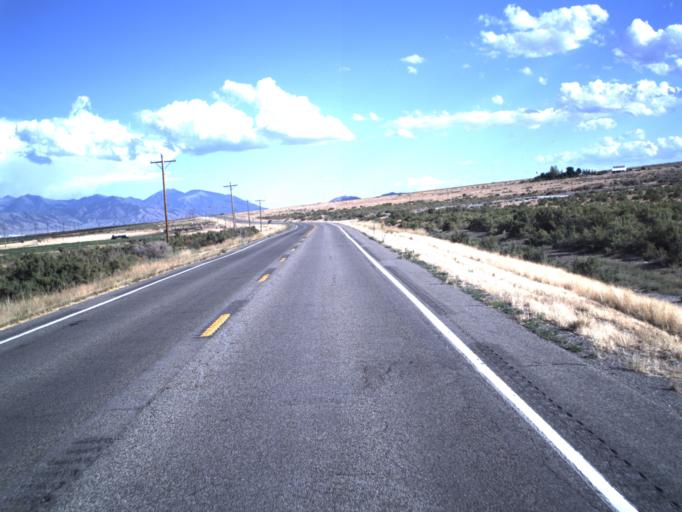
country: US
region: Utah
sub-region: Tooele County
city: Grantsville
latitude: 40.6429
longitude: -112.5260
